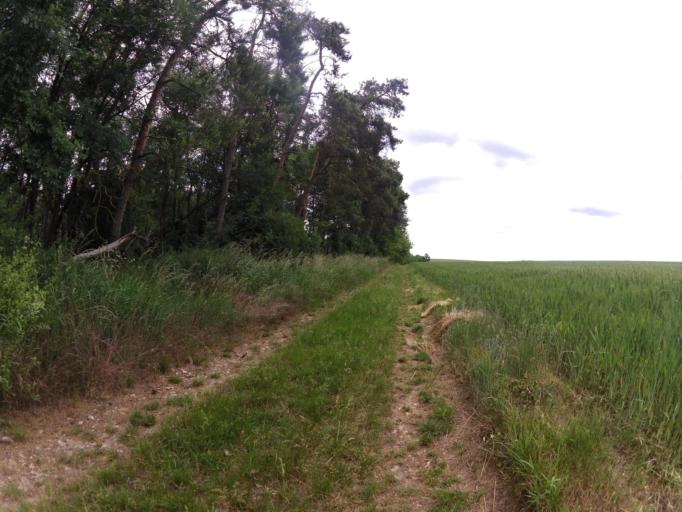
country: DE
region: Bavaria
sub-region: Regierungsbezirk Unterfranken
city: Gaukonigshofen
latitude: 49.6661
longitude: 9.9945
